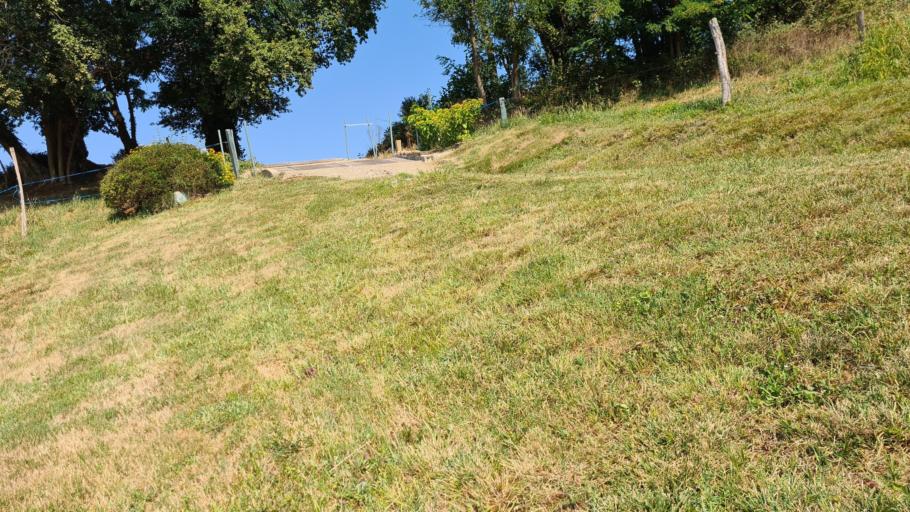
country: FR
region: Aquitaine
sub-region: Departement des Pyrenees-Atlantiques
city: Ledeuix
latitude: 43.2180
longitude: -0.5905
